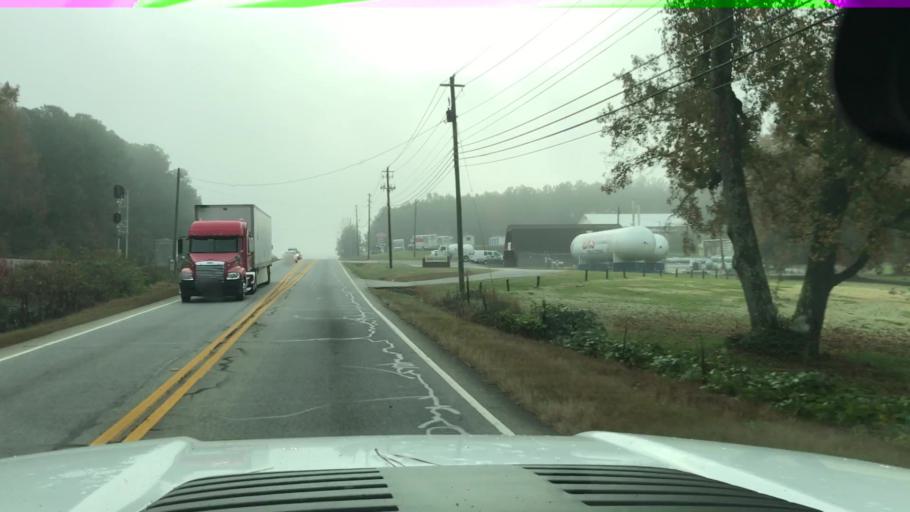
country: US
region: Georgia
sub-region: Barrow County
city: Russell
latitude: 33.9746
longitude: -83.6944
